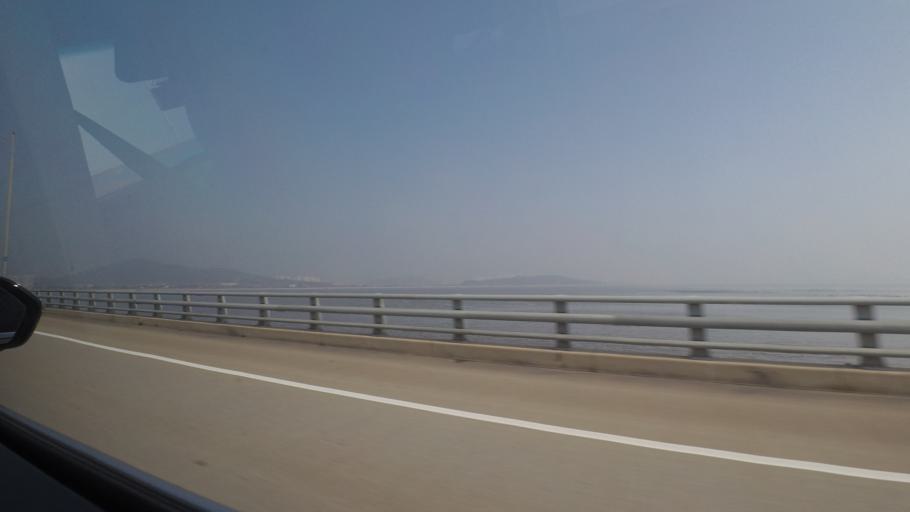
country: KR
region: Incheon
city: Incheon
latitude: 37.4553
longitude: 126.5237
